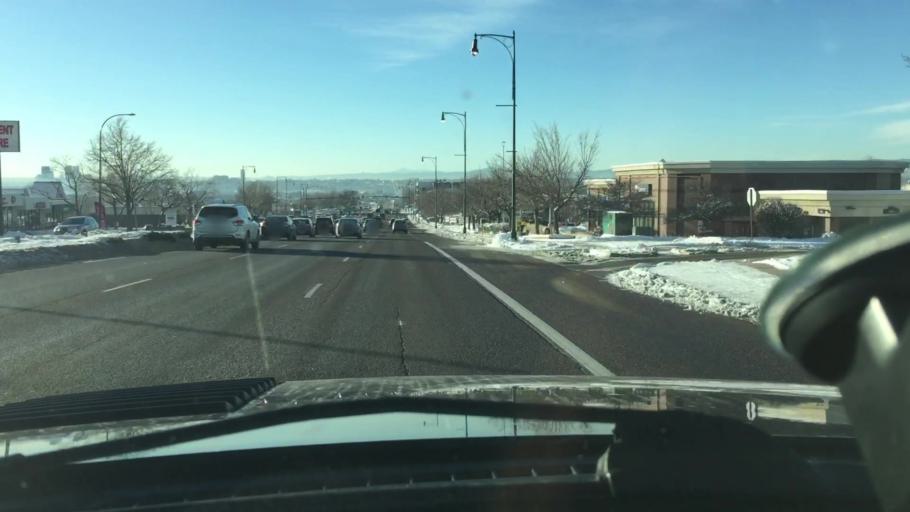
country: US
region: Colorado
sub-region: Adams County
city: Westminster
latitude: 39.8304
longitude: -105.0251
